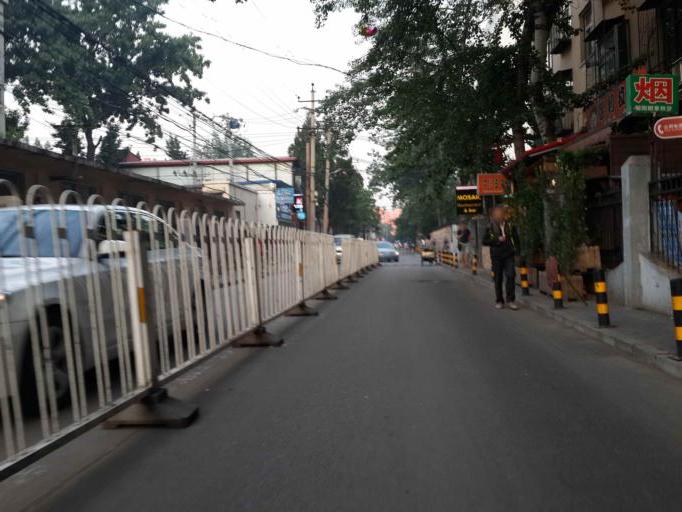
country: CN
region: Beijing
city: Chaowai
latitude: 39.9345
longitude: 116.4458
